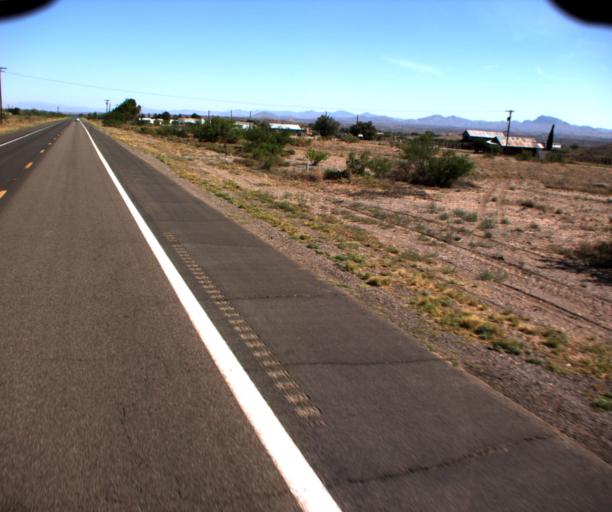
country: US
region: Arizona
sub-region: Greenlee County
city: Clifton
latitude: 32.6710
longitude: -109.0764
